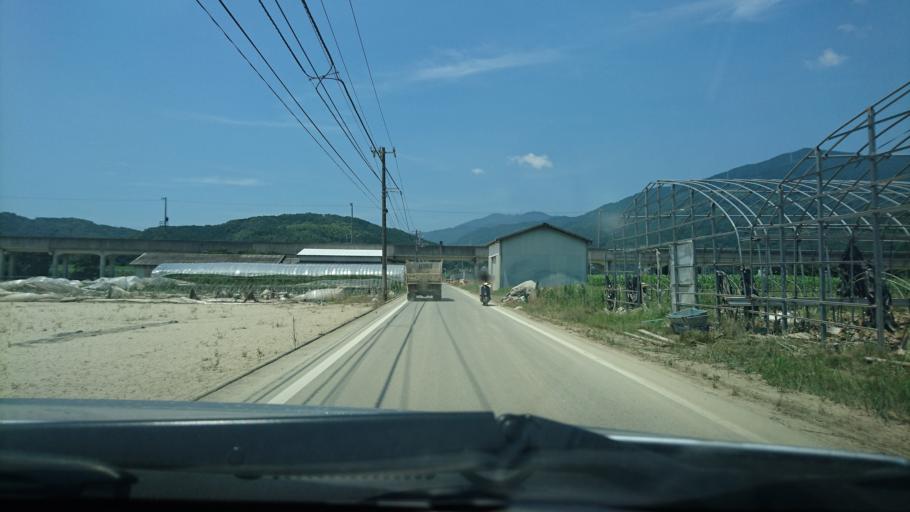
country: JP
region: Ehime
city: Ozu
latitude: 33.5323
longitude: 132.5679
